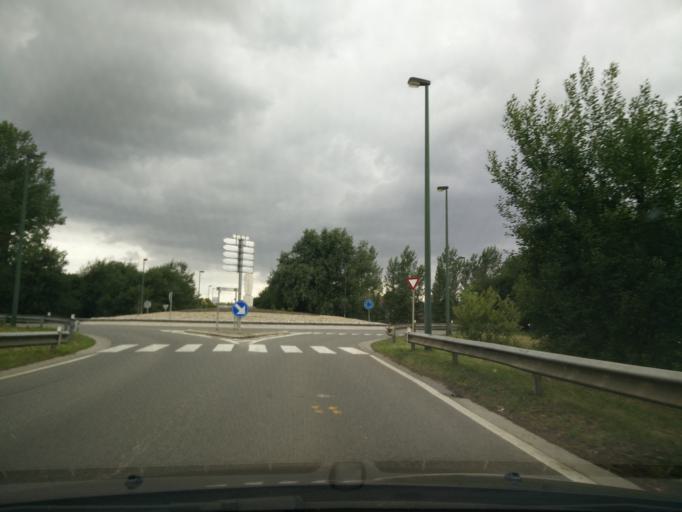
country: BE
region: Wallonia
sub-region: Province de Liege
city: Bassenge
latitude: 50.7787
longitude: 5.6580
